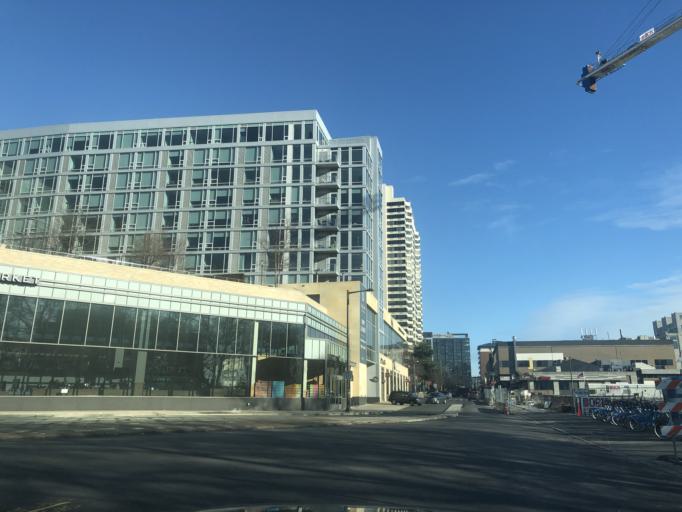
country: US
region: Pennsylvania
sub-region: Philadelphia County
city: Philadelphia
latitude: 39.9625
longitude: -75.1738
